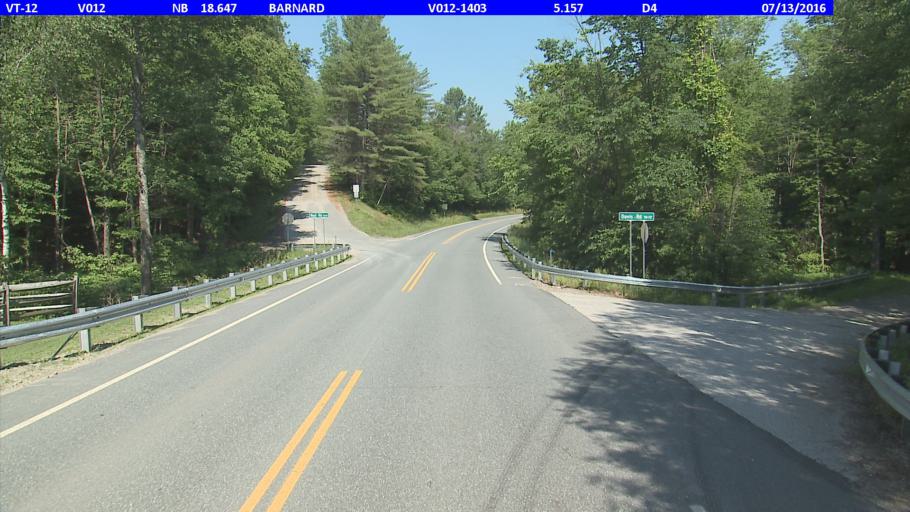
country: US
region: Vermont
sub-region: Windsor County
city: Woodstock
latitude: 43.7328
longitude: -72.6235
